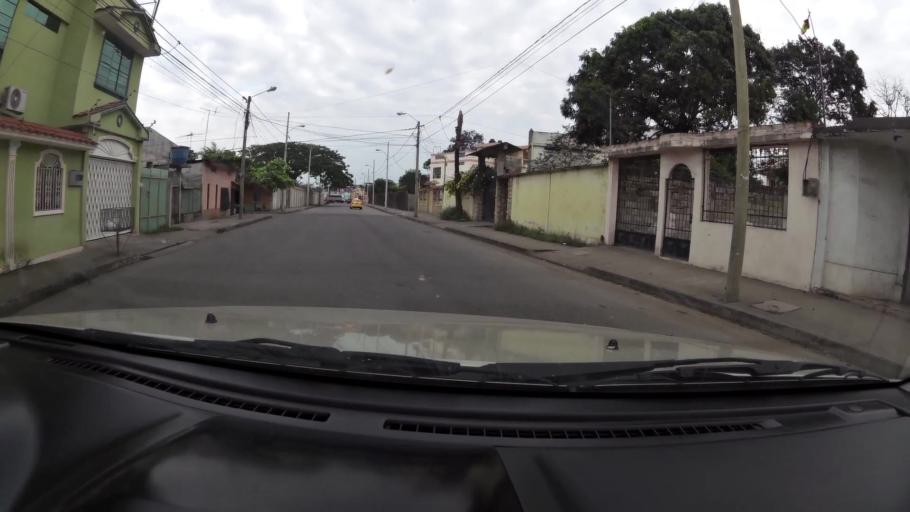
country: EC
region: El Oro
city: Machala
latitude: -3.2653
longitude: -79.9459
